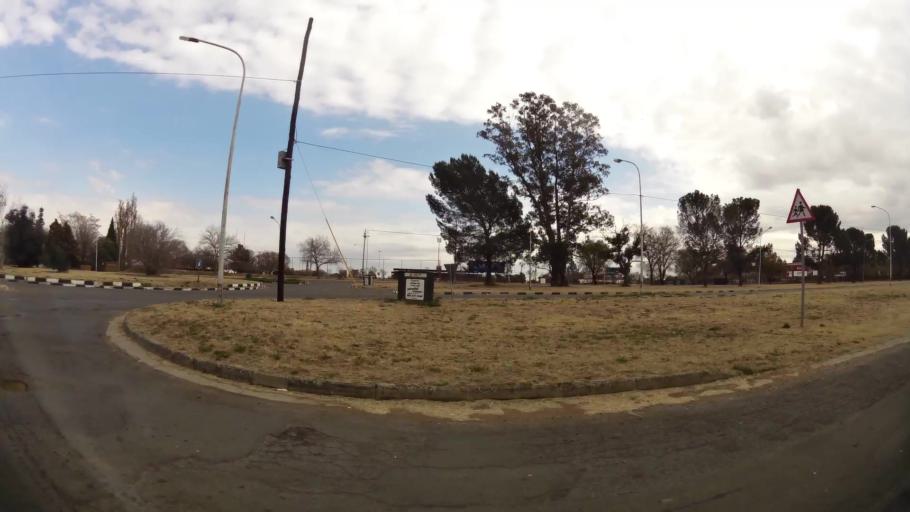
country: ZA
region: Orange Free State
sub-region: Fezile Dabi District Municipality
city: Kroonstad
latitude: -27.6390
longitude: 27.2340
